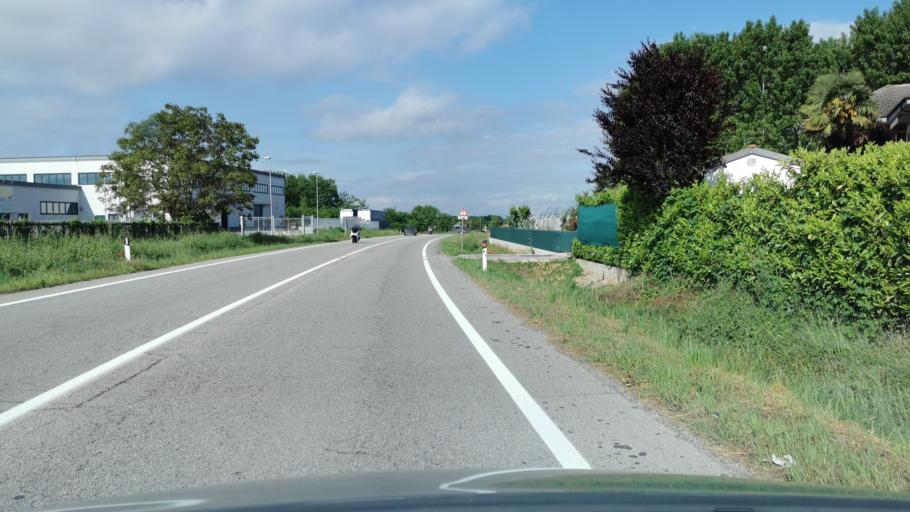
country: IT
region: Piedmont
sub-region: Provincia di Torino
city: Santena
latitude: 44.9397
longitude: 7.7770
